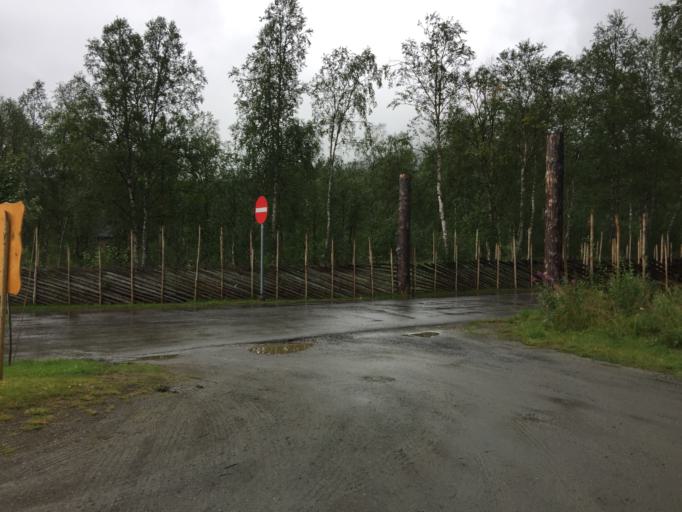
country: NO
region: Troms
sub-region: Bardu
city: Setermoen
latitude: 68.6921
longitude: 18.1112
